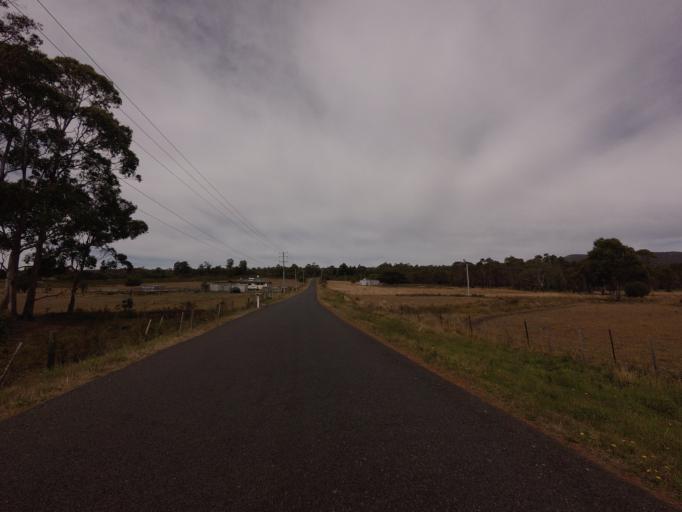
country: AU
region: Tasmania
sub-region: Sorell
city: Sorell
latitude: -42.5635
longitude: 147.5717
